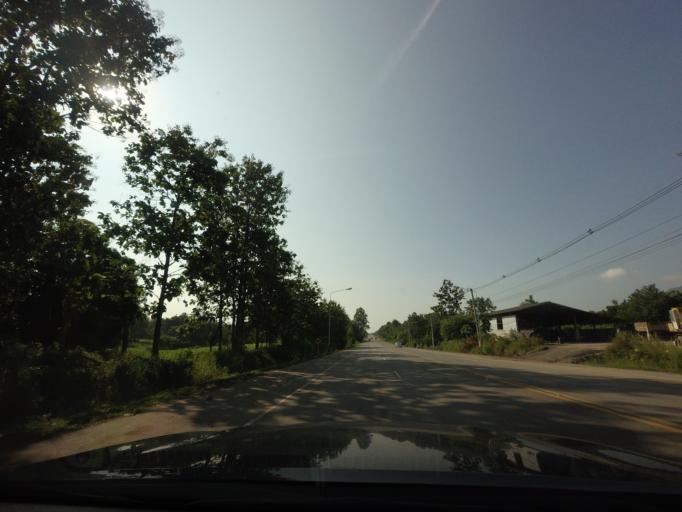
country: TH
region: Phetchabun
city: Lom Kao
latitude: 16.8620
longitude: 101.1718
